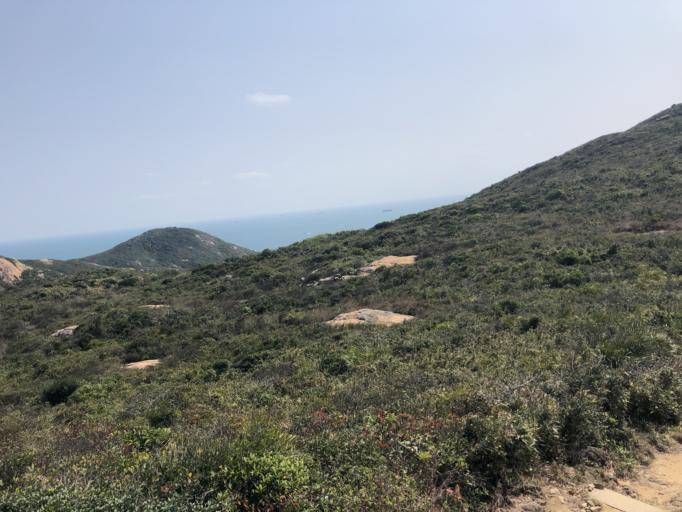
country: HK
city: Sok Kwu Wan
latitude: 22.1678
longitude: 114.2609
